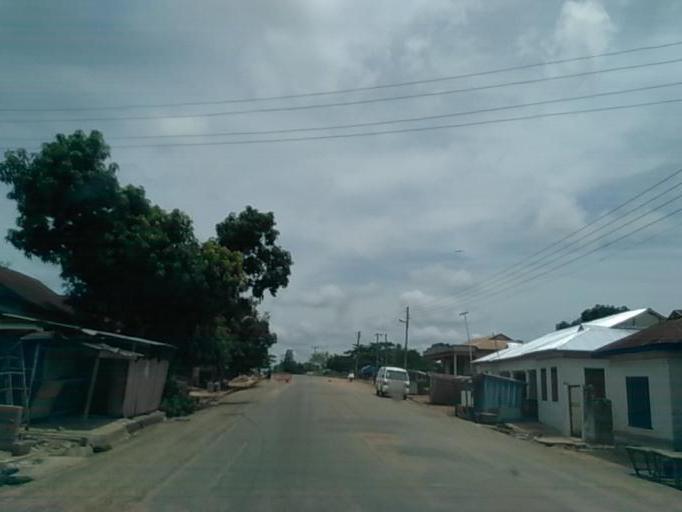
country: GH
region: Ashanti
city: Mamponteng
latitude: 6.8288
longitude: -1.4975
